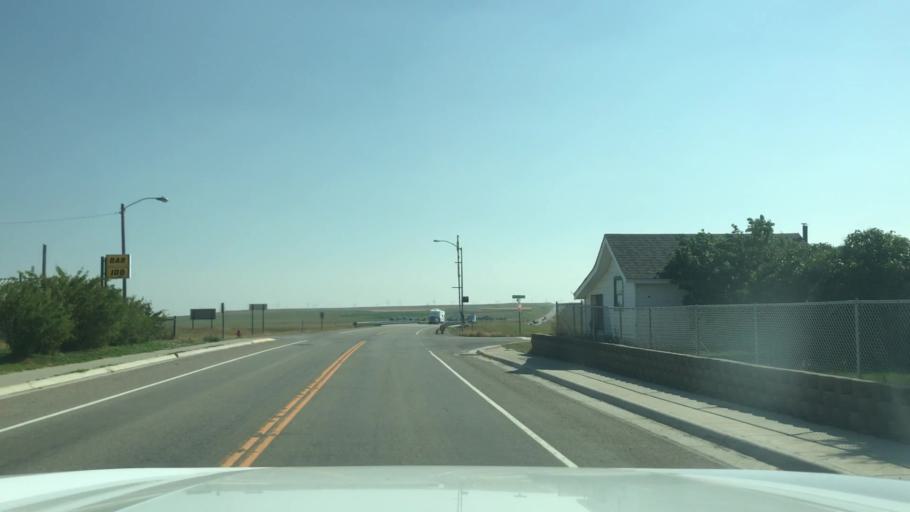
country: US
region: Montana
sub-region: Wheatland County
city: Harlowton
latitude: 46.6757
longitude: -109.7524
